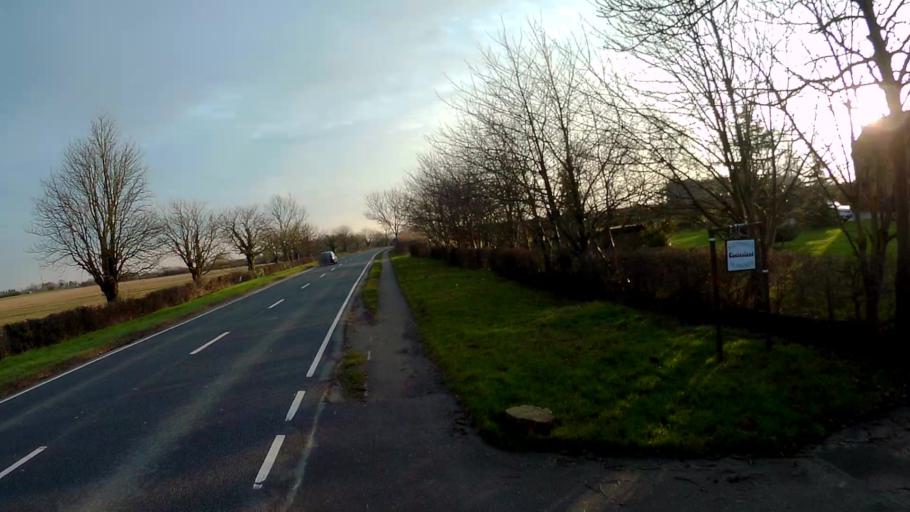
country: GB
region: England
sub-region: Lincolnshire
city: Bourne
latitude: 52.7963
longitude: -0.3770
